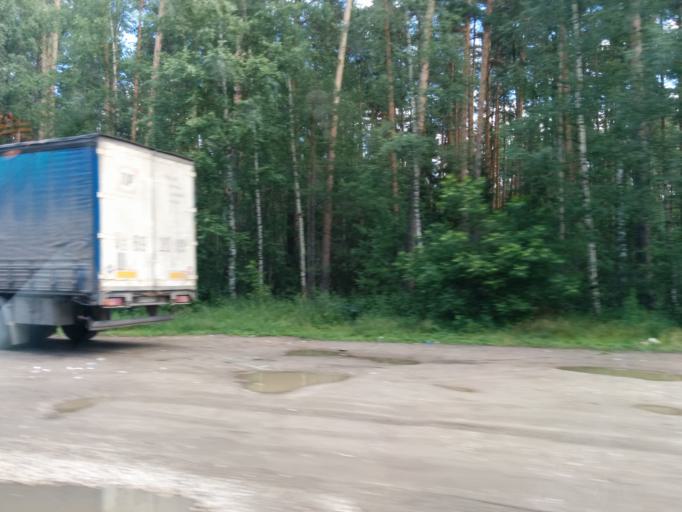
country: RU
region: Perm
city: Perm
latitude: 58.0453
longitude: 56.1852
